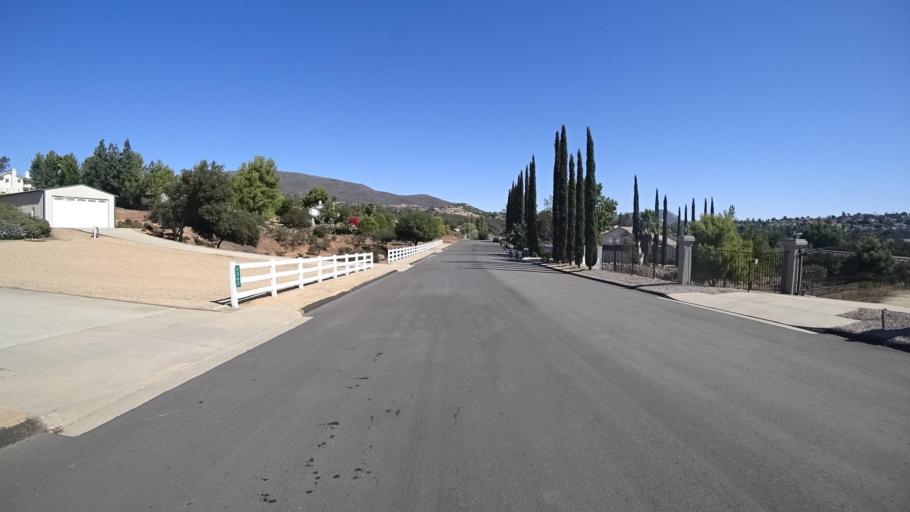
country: US
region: California
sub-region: San Diego County
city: Alpine
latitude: 32.8401
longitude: -116.7656
